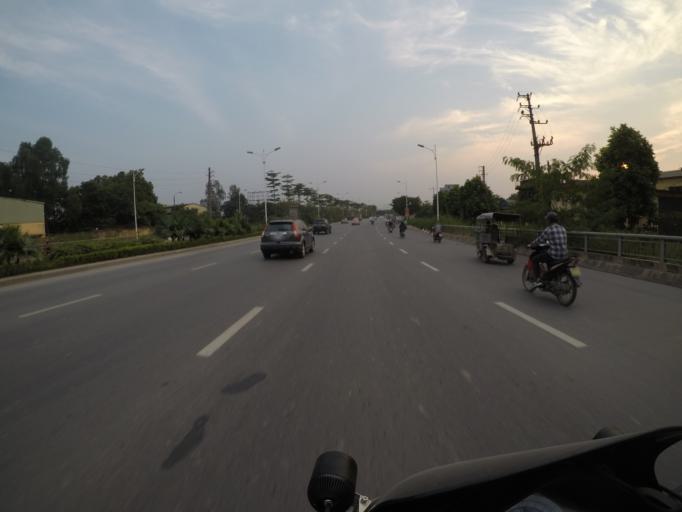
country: VN
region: Ha Noi
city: Trau Quy
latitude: 21.0336
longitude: 105.9013
